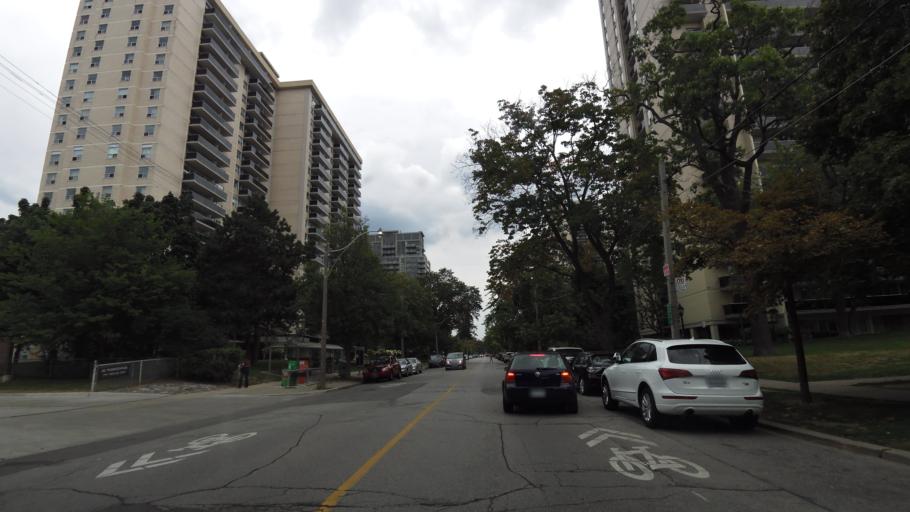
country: CA
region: Ontario
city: Toronto
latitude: 43.6541
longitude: -79.4655
